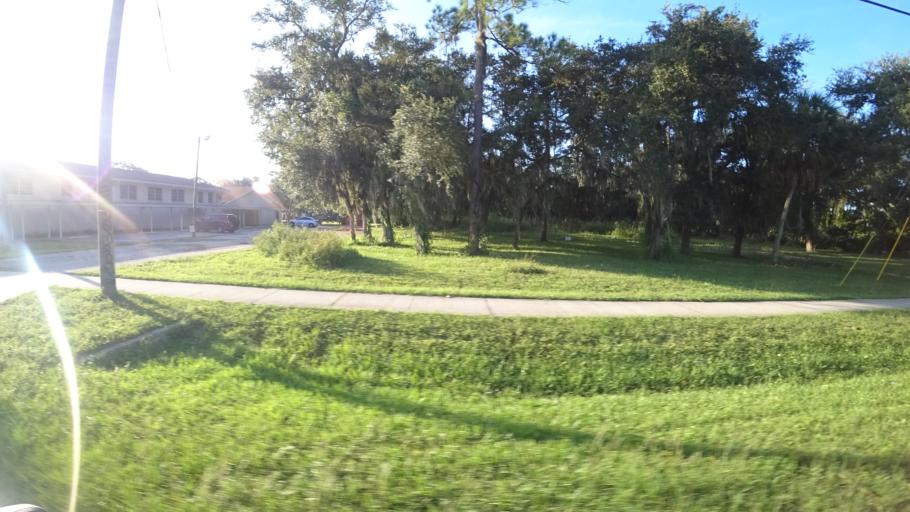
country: US
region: Florida
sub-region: Manatee County
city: Samoset
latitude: 27.4512
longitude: -82.5441
